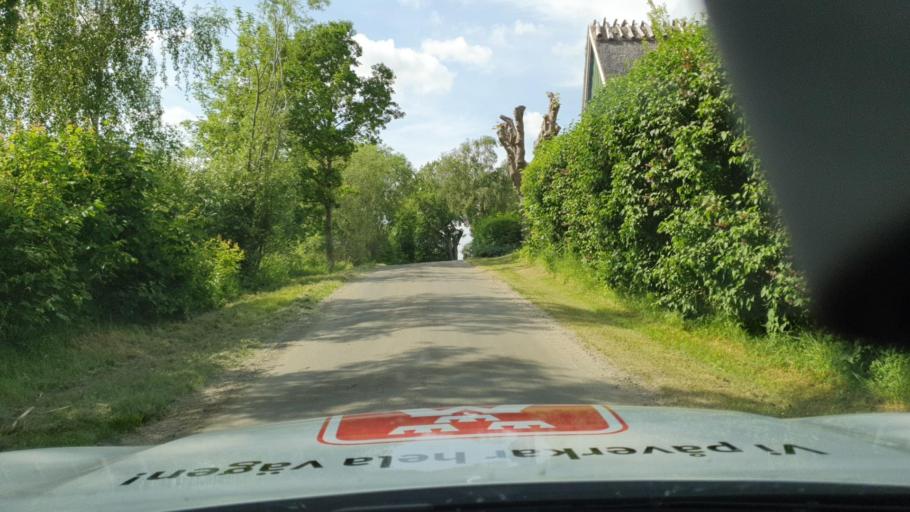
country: SE
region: Skane
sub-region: Skurups Kommun
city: Skurup
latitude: 55.5366
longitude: 13.5351
